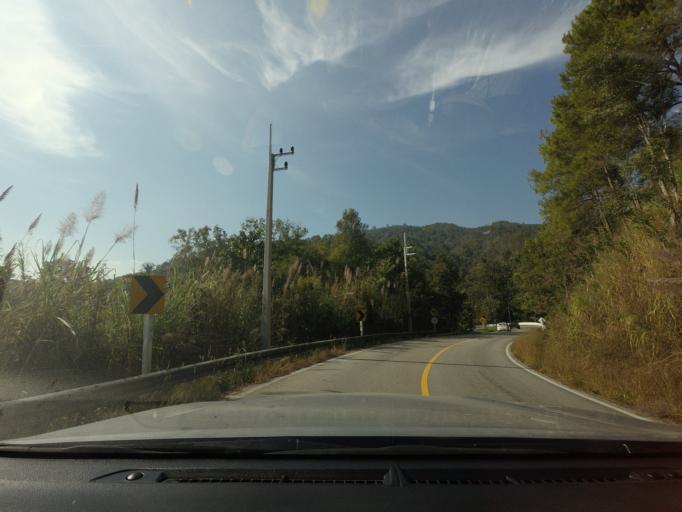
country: TH
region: Mae Hong Son
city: Mae Hi
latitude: 19.2195
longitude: 98.6706
